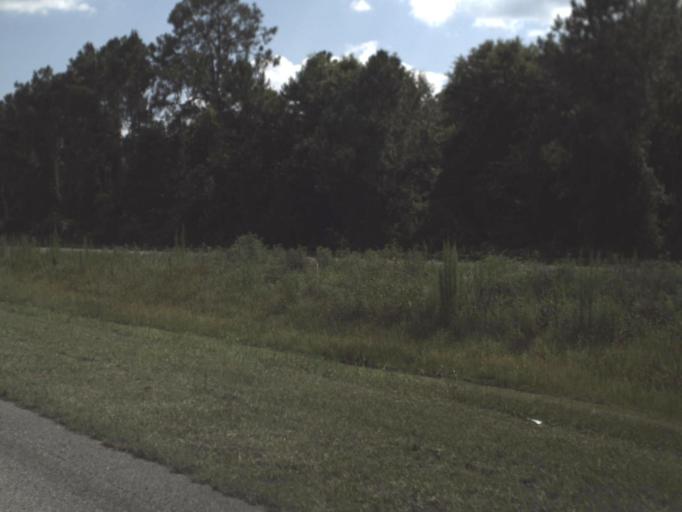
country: US
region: Florida
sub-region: Alachua County
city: Hawthorne
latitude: 29.5327
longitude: -82.1016
